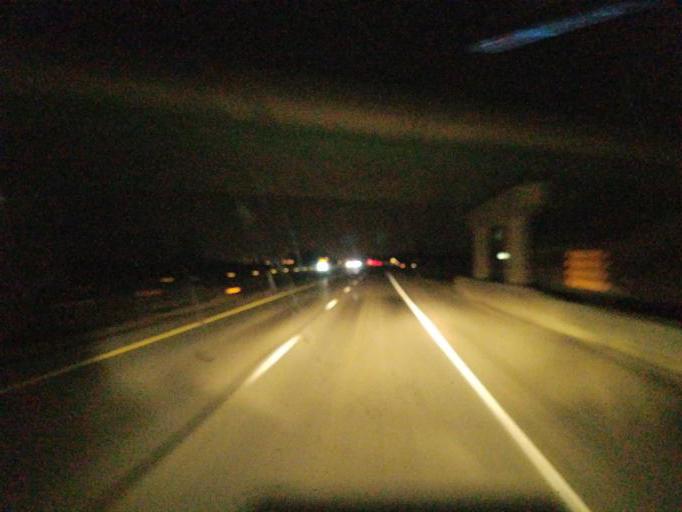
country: US
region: Iowa
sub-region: Madison County
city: Earlham
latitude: 41.5197
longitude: -94.0777
